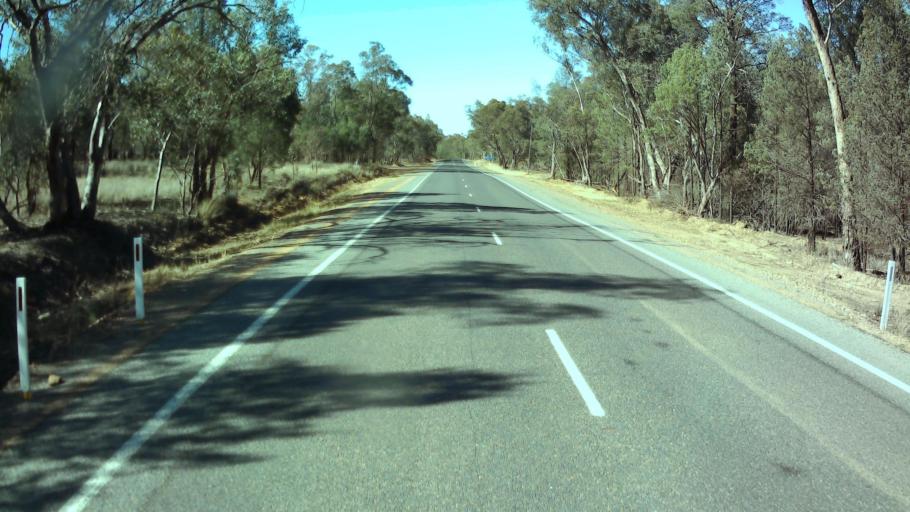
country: AU
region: New South Wales
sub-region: Weddin
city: Grenfell
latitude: -33.7489
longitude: 148.0862
